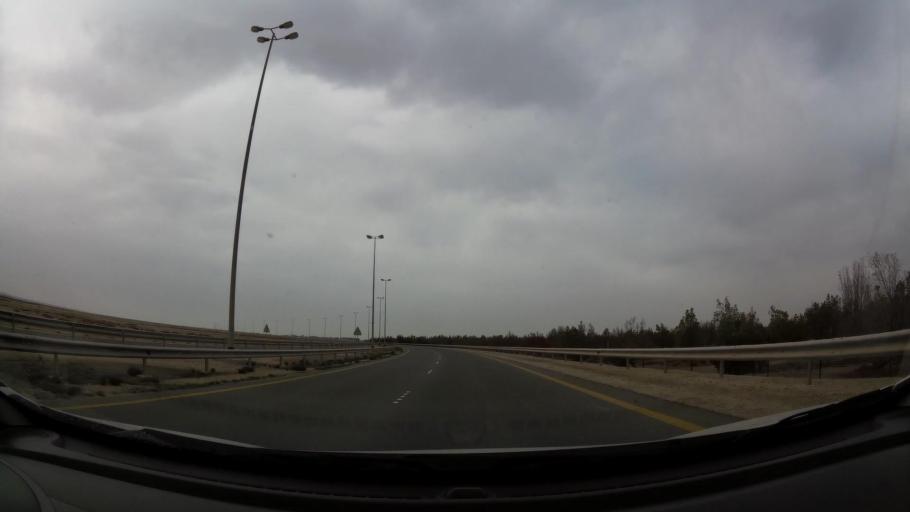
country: BH
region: Central Governorate
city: Dar Kulayb
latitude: 26.0144
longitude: 50.4842
